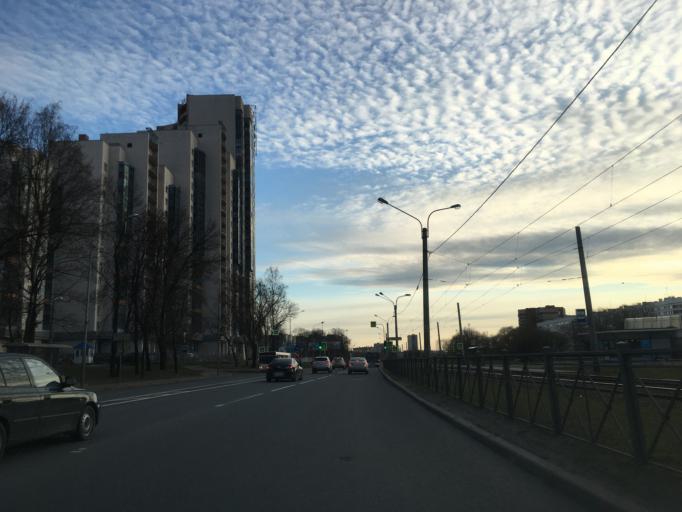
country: RU
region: St.-Petersburg
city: Dachnoye
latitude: 59.8546
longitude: 30.2442
